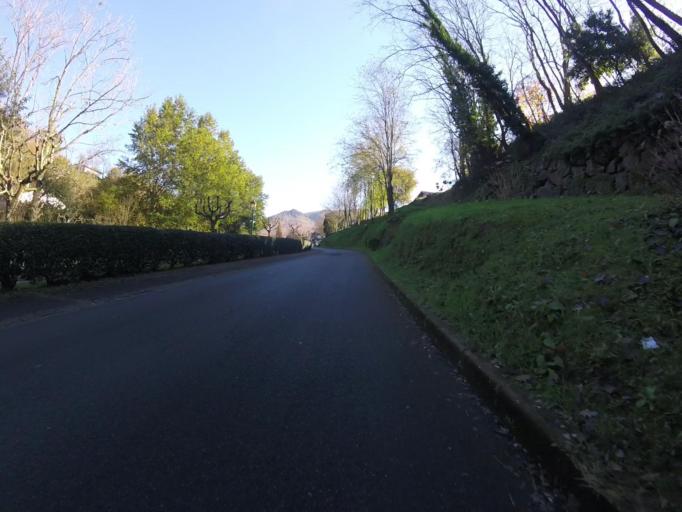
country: ES
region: Basque Country
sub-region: Provincia de Guipuzcoa
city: Irun
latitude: 43.3341
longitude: -1.7474
